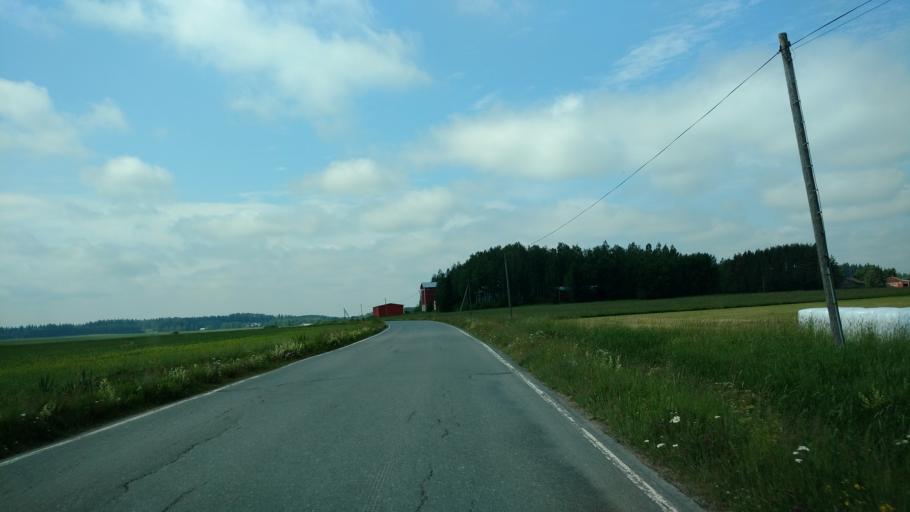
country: FI
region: Haeme
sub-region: Forssa
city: Jokioinen
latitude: 60.7900
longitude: 23.3976
